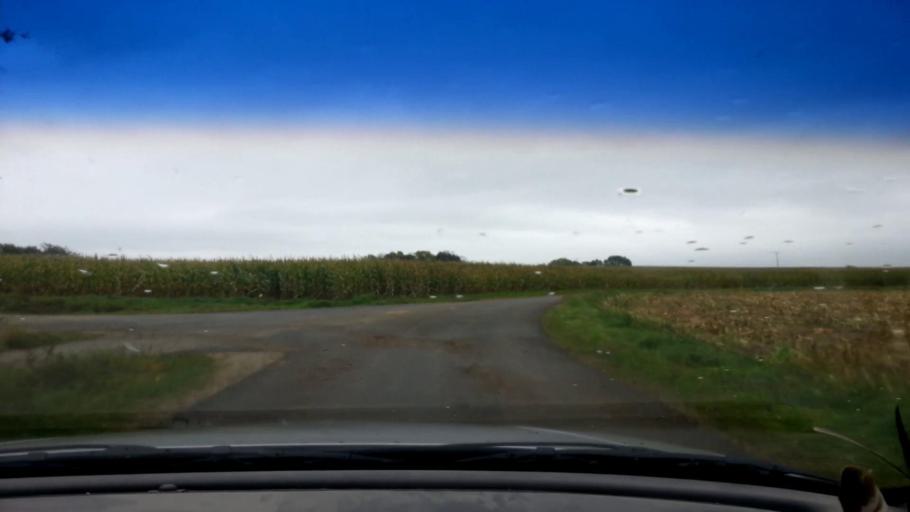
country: DE
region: Bavaria
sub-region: Upper Franconia
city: Poxdorf
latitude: 49.8968
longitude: 11.0832
